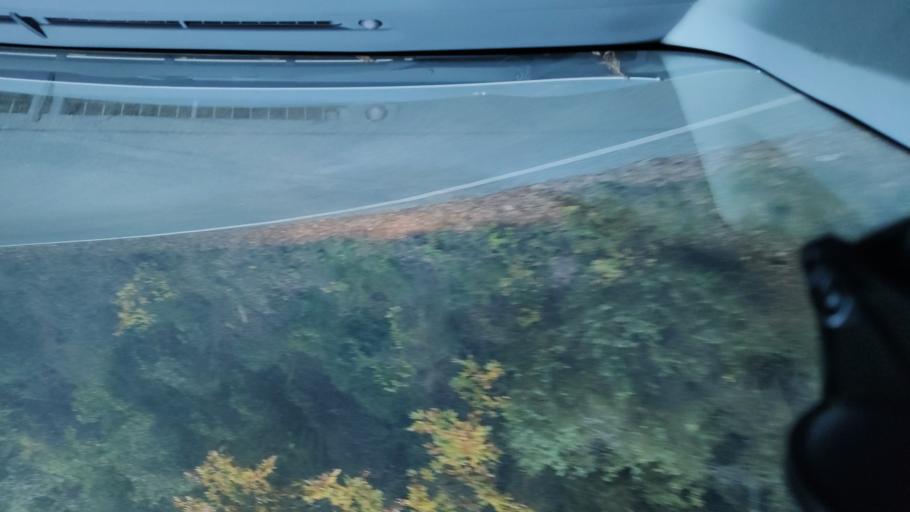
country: IT
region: Umbria
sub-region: Provincia di Terni
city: Amelia
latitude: 42.5882
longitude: 12.4303
